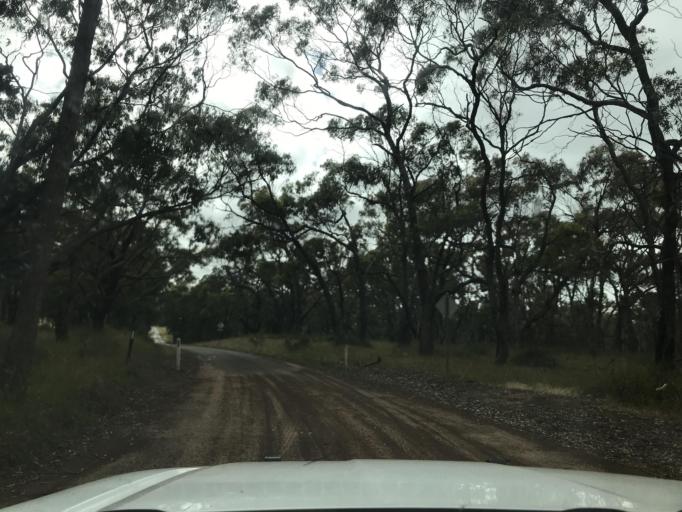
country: AU
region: South Australia
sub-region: Wattle Range
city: Penola
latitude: -37.3418
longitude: 141.4316
